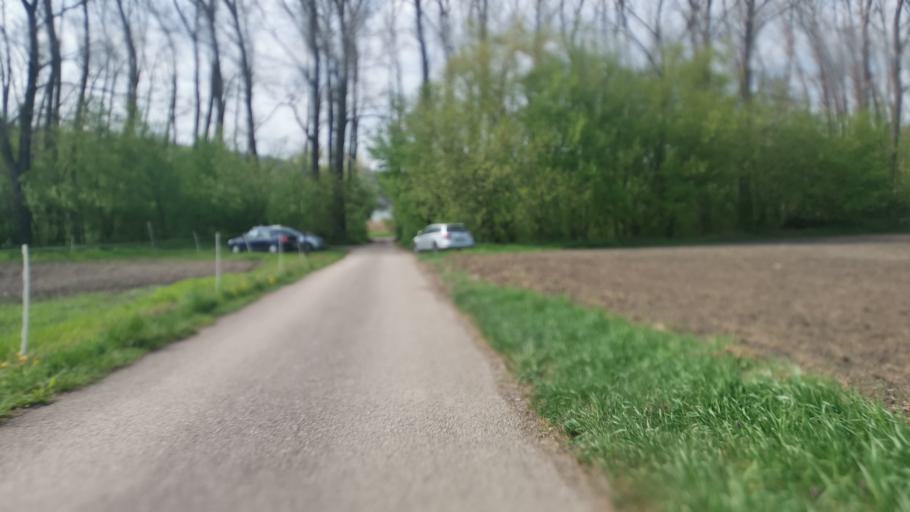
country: SK
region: Trnavsky
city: Smolenice
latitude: 48.5315
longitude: 17.3654
